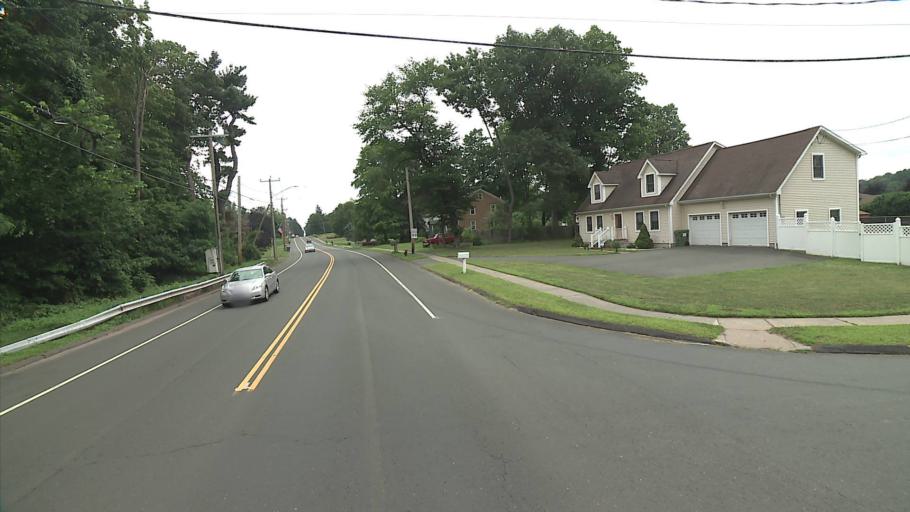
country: US
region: Connecticut
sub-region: Middlesex County
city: Cromwell
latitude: 41.6135
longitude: -72.6525
